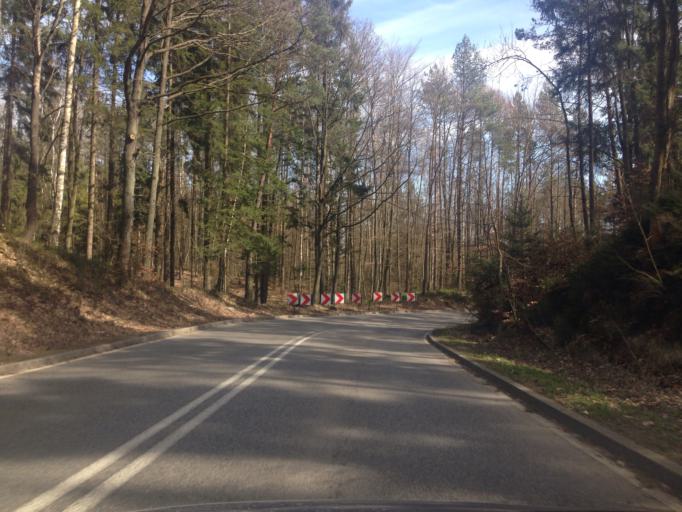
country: PL
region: Pomeranian Voivodeship
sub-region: Gdynia
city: Wielki Kack
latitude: 54.4776
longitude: 18.4526
